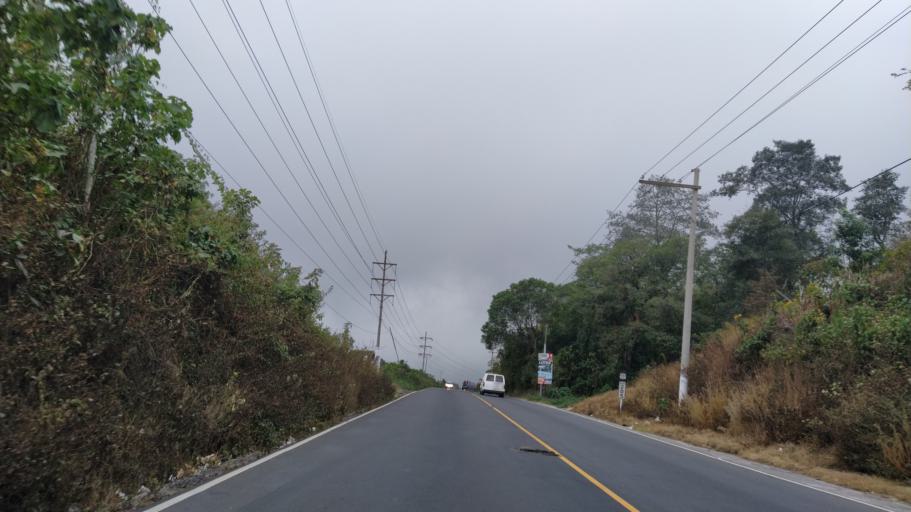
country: GT
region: Quetzaltenango
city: Zunil
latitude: 14.7361
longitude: -91.5216
